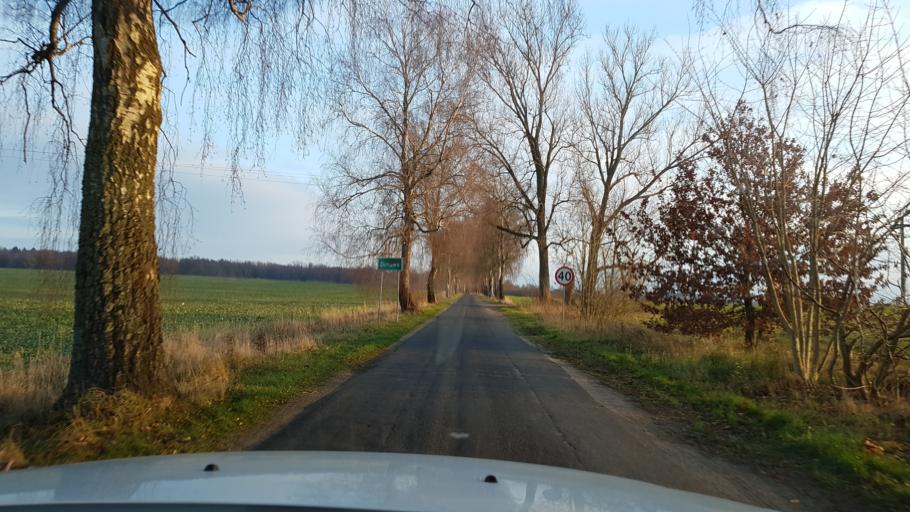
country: PL
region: West Pomeranian Voivodeship
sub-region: Koszalin
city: Koszalin
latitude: 54.1119
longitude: 16.1169
